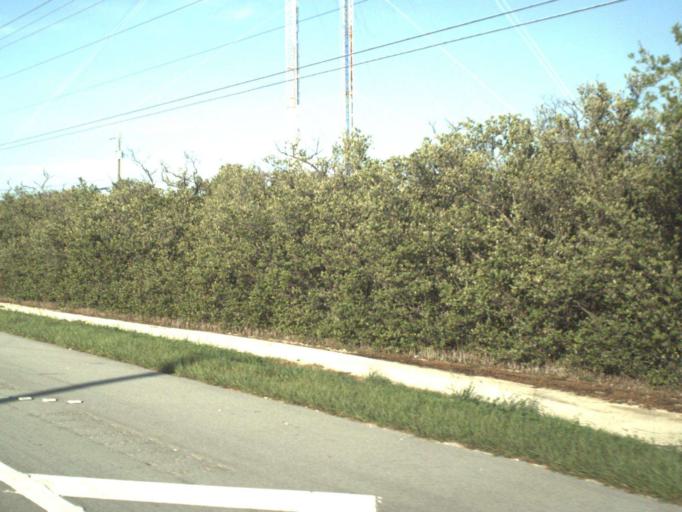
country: US
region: Florida
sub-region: Monroe County
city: Islamorada
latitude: 24.8128
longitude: -80.8270
